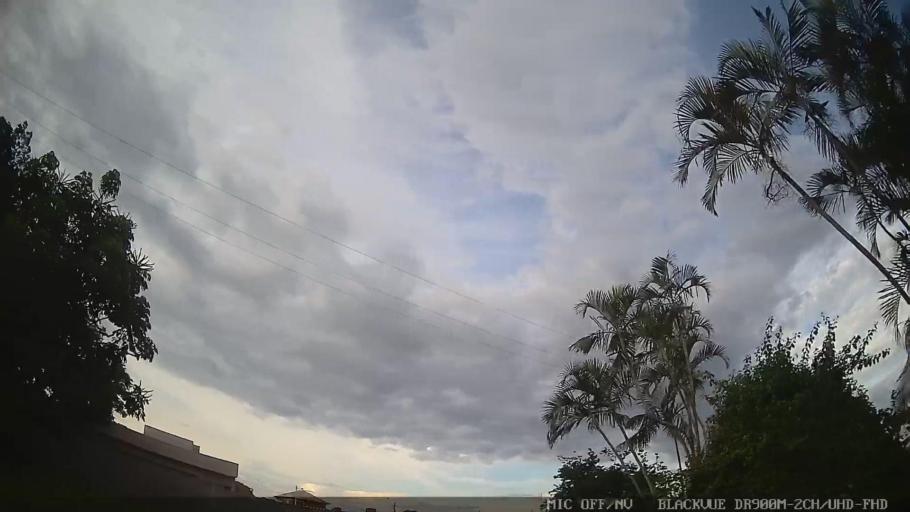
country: BR
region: Sao Paulo
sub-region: Jaguariuna
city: Jaguariuna
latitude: -22.6333
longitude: -47.0477
